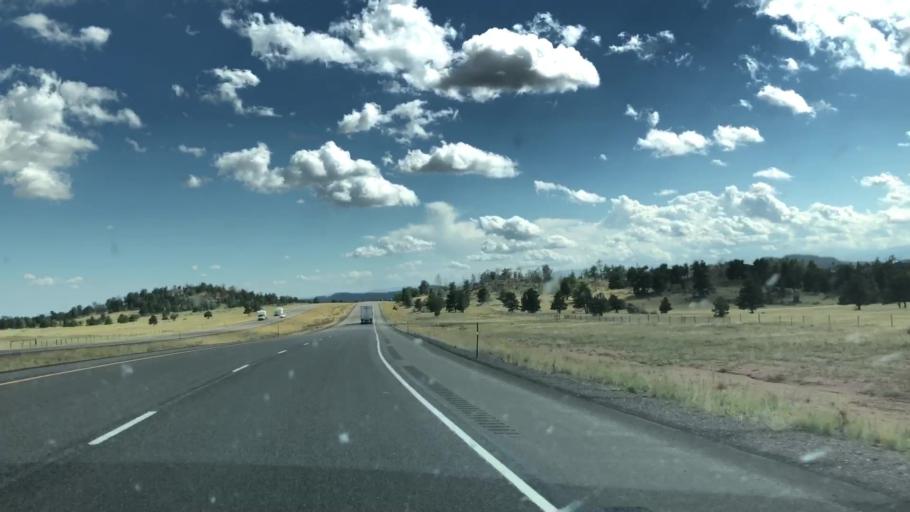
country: US
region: Wyoming
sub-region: Albany County
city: Laramie
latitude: 41.0184
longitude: -105.4212
